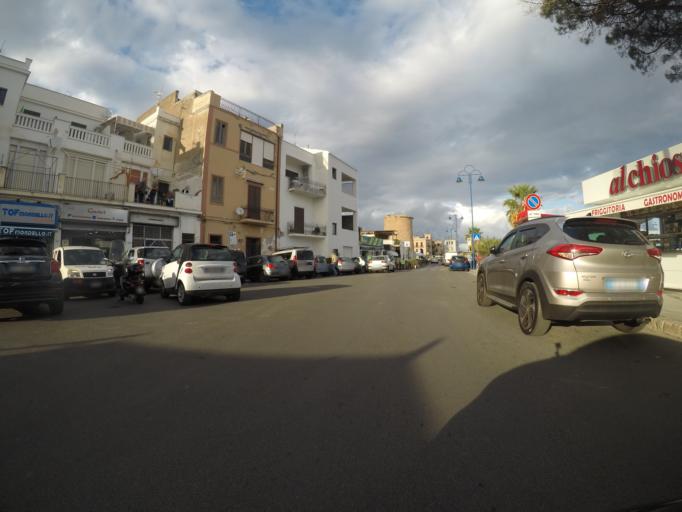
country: IT
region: Sicily
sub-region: Palermo
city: Palermo
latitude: 38.2066
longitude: 13.3255
